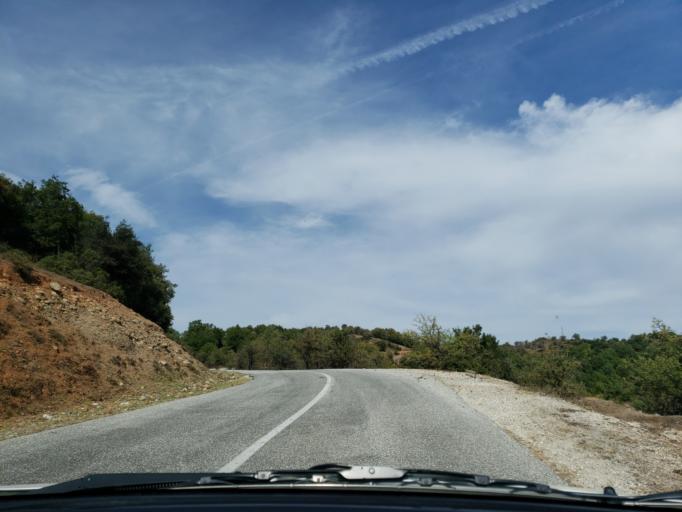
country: GR
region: Thessaly
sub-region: Trikala
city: Kastraki
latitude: 39.7279
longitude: 21.6484
